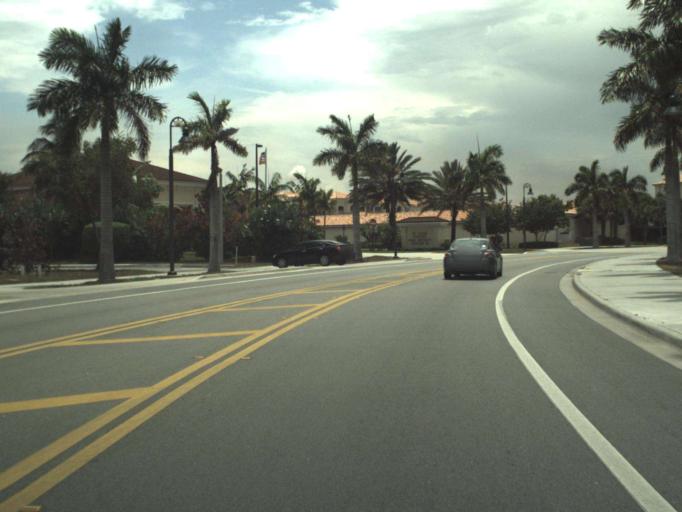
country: US
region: Florida
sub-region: Saint Lucie County
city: Fort Pierce
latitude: 27.4633
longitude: -80.3030
